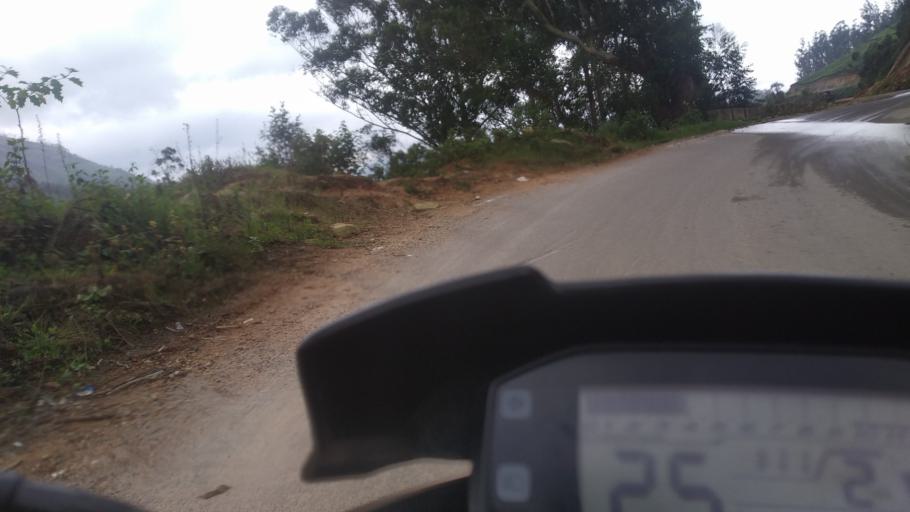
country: IN
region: Kerala
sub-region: Idukki
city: Munnar
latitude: 10.0826
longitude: 77.0735
